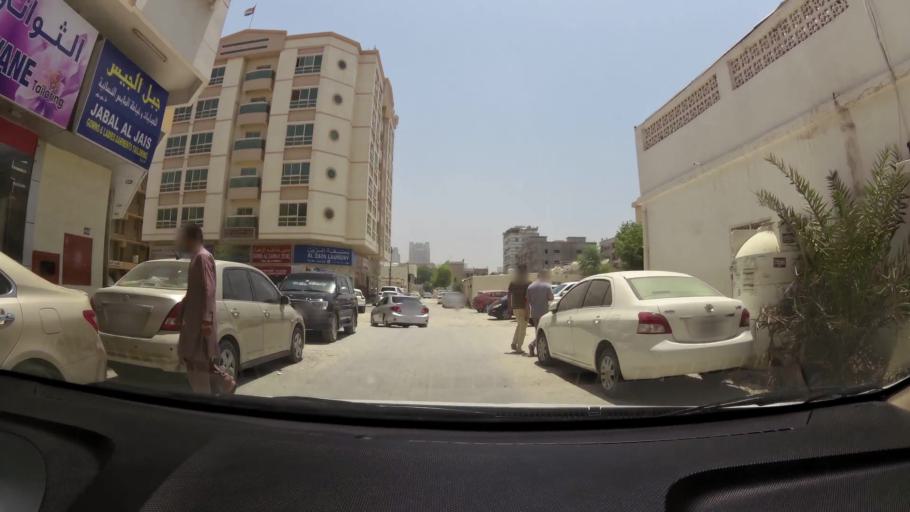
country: AE
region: Ajman
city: Ajman
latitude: 25.4039
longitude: 55.4393
